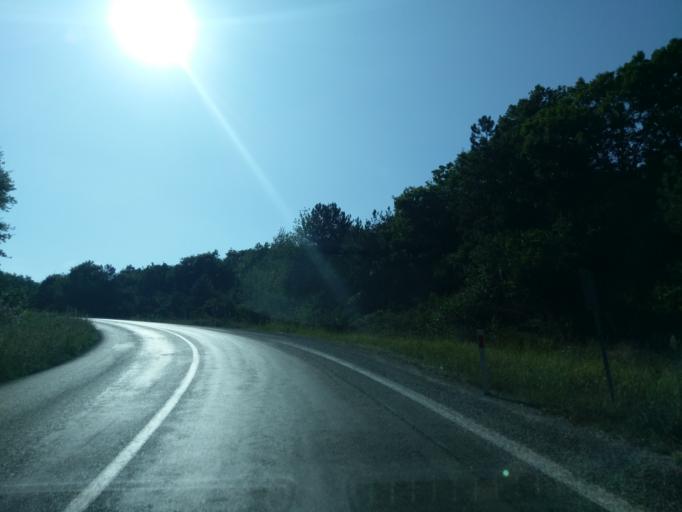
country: TR
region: Sinop
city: Yenikonak
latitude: 41.9467
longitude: 34.7438
